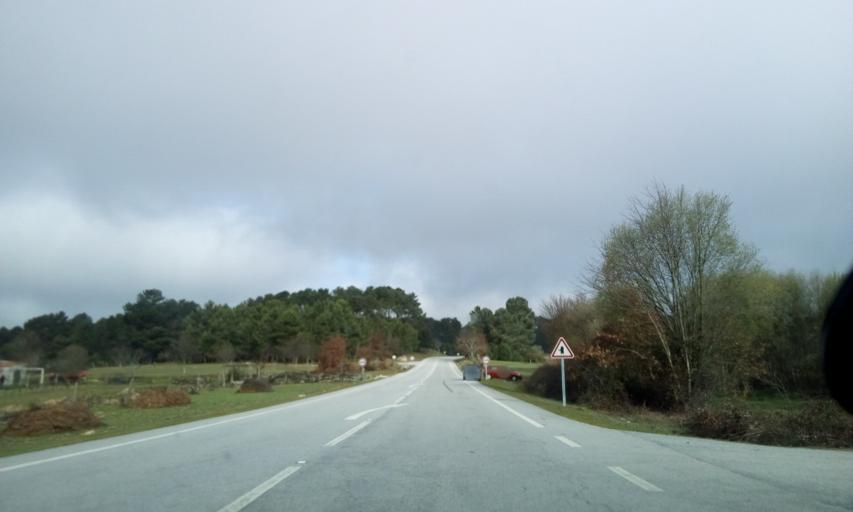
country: PT
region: Guarda
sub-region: Aguiar da Beira
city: Aguiar da Beira
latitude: 40.7467
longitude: -7.5024
